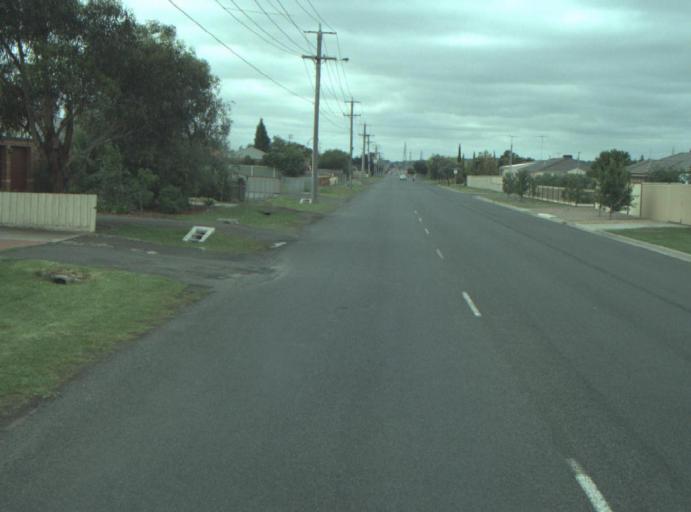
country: AU
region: Victoria
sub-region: Greater Geelong
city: Bell Post Hill
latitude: -38.0661
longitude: 144.3402
